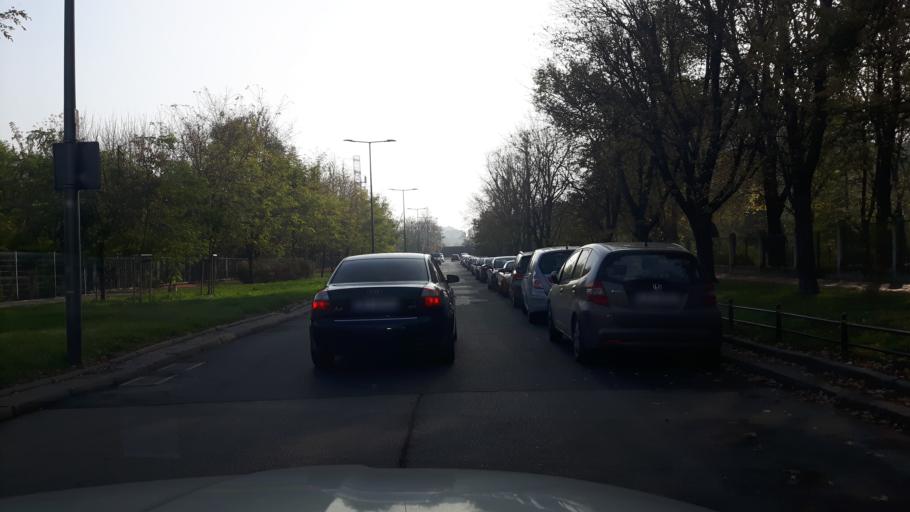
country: PL
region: Masovian Voivodeship
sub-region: Warszawa
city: Ochota
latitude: 52.1904
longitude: 20.9955
